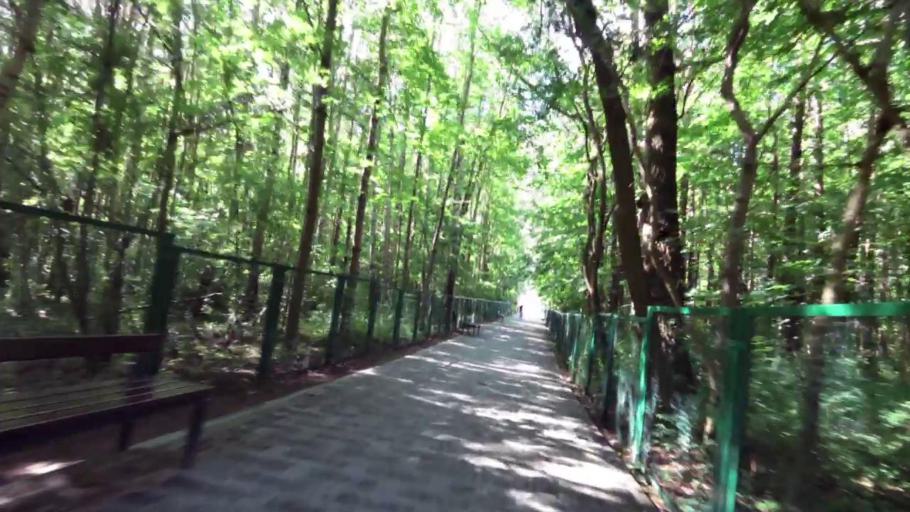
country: PL
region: West Pomeranian Voivodeship
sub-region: Powiat koszalinski
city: Mielno
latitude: 54.2650
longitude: 16.0678
